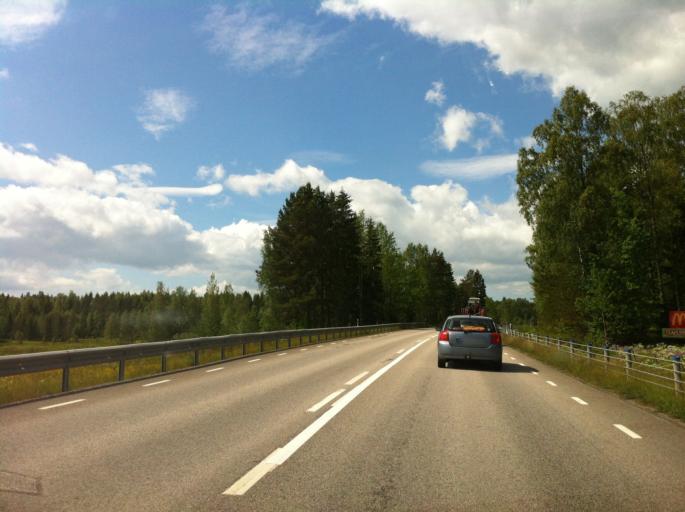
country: SE
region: Vaermland
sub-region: Saffle Kommun
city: Saeffle
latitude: 59.1530
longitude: 12.9721
